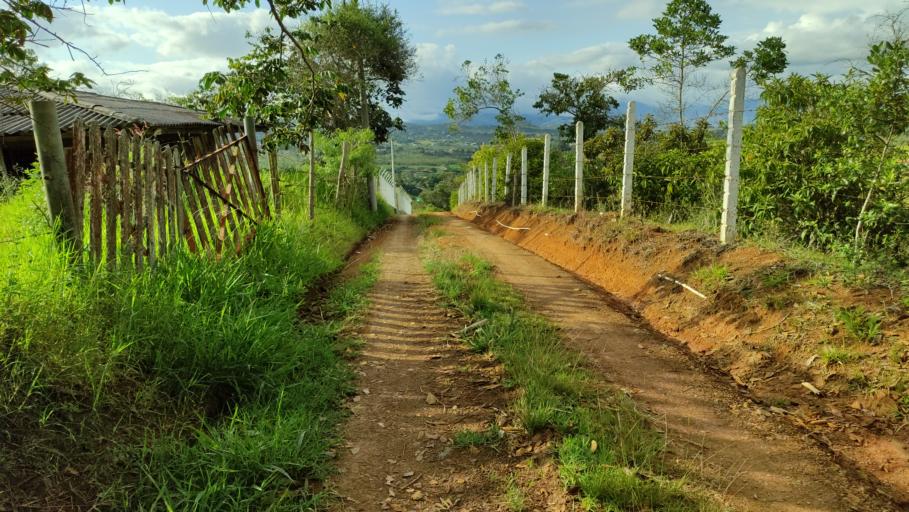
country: CO
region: Valle del Cauca
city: Dagua
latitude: 3.5370
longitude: -76.6438
